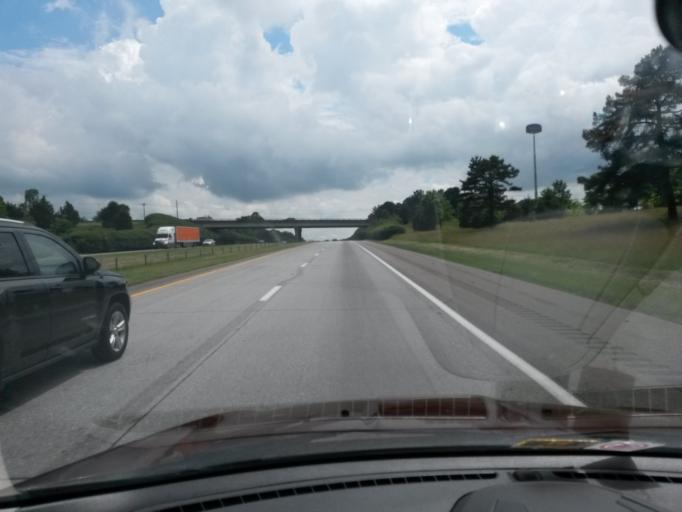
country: US
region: North Carolina
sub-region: Surry County
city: Elkin
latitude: 36.2819
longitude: -80.8211
